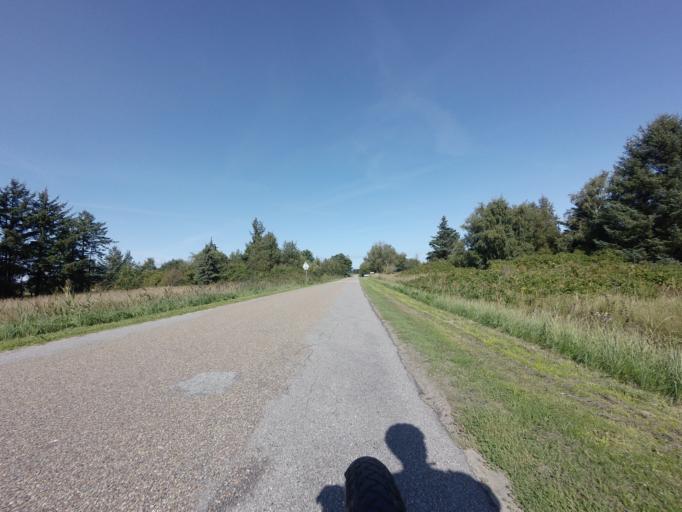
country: DK
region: North Denmark
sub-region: Hjorring Kommune
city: Hirtshals
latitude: 57.5821
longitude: 10.0284
